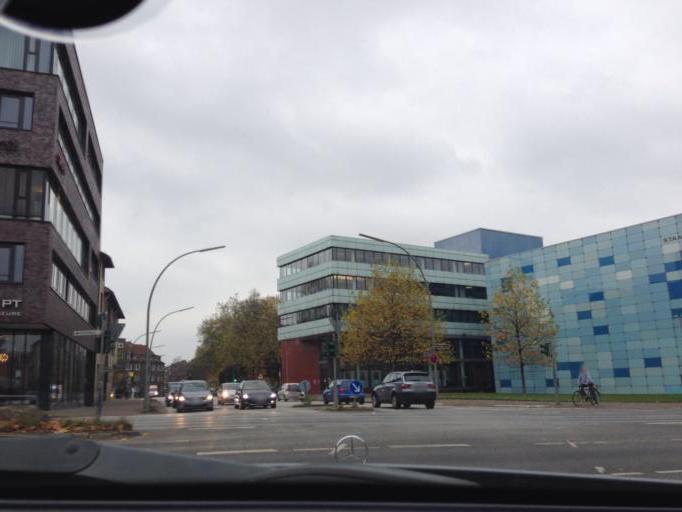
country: DE
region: Hamburg
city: Marienthal
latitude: 53.5747
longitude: 10.0701
